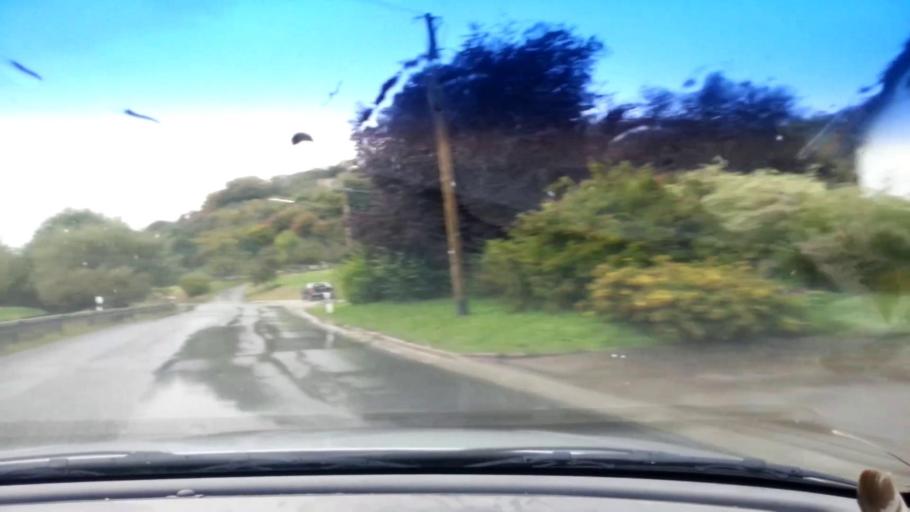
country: DE
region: Bavaria
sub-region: Upper Franconia
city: Wattendorf
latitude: 50.0148
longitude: 11.0779
